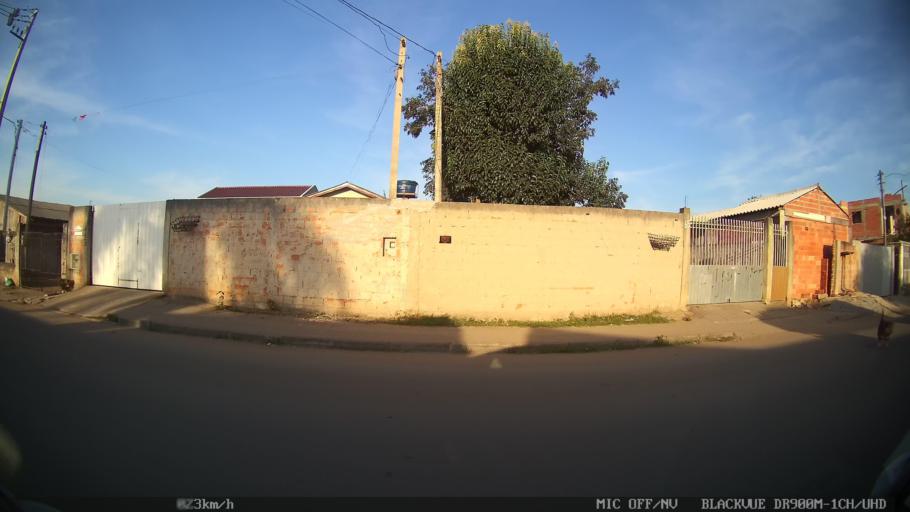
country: BR
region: Parana
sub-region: Pinhais
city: Pinhais
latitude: -25.4545
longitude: -49.1456
